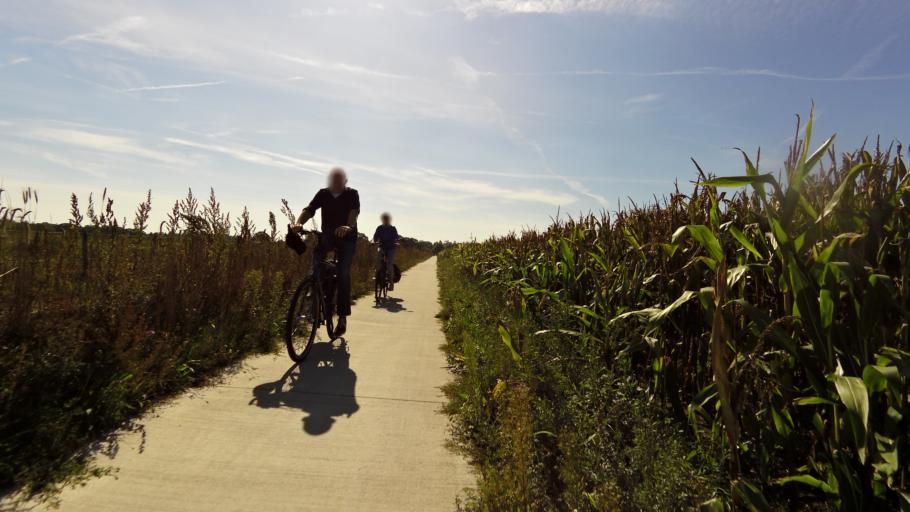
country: NL
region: Gelderland
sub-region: Gemeente Renkum
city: Heelsum
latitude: 51.9951
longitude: 5.7431
